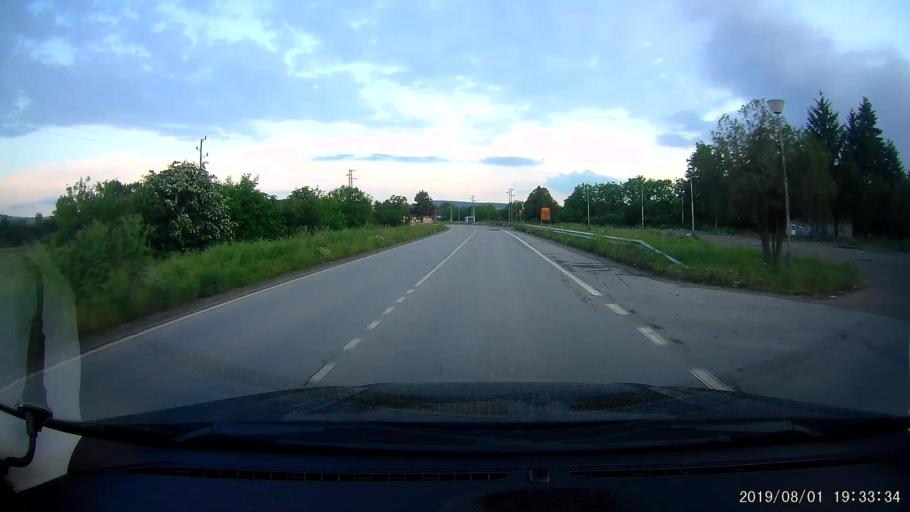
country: BG
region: Burgas
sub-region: Obshtina Sungurlare
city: Sungurlare
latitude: 42.7779
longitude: 26.8769
